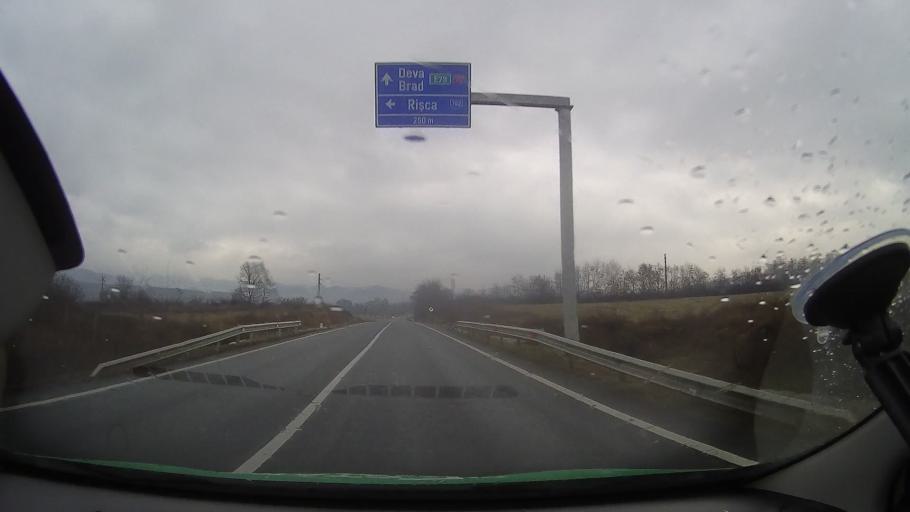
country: RO
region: Hunedoara
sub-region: Comuna Baia de Cris
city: Baia de Cris
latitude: 46.1701
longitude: 22.7221
